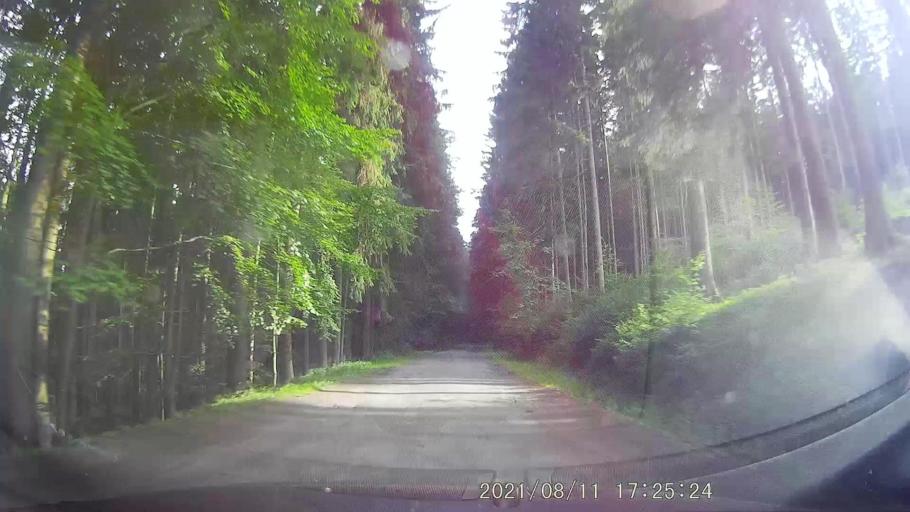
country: PL
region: Lower Silesian Voivodeship
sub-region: Powiat klodzki
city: Polanica-Zdroj
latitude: 50.3074
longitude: 16.4965
